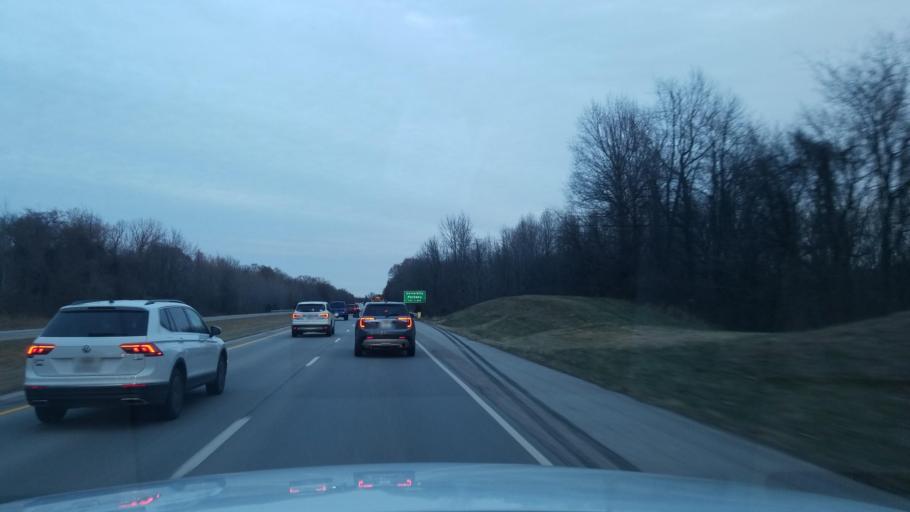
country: US
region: Indiana
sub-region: Vanderburgh County
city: Evansville
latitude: 37.9550
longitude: -87.6956
